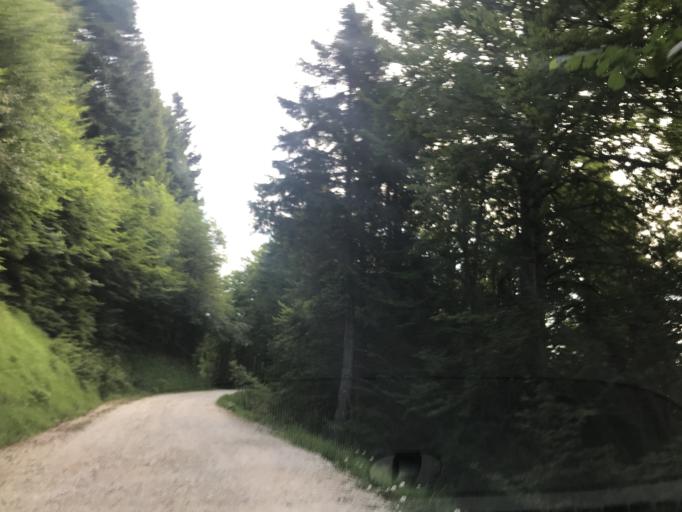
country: FR
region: Rhone-Alpes
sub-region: Departement de l'Isere
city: Saint-Vincent-de-Mercuze
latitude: 45.4143
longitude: 5.9366
